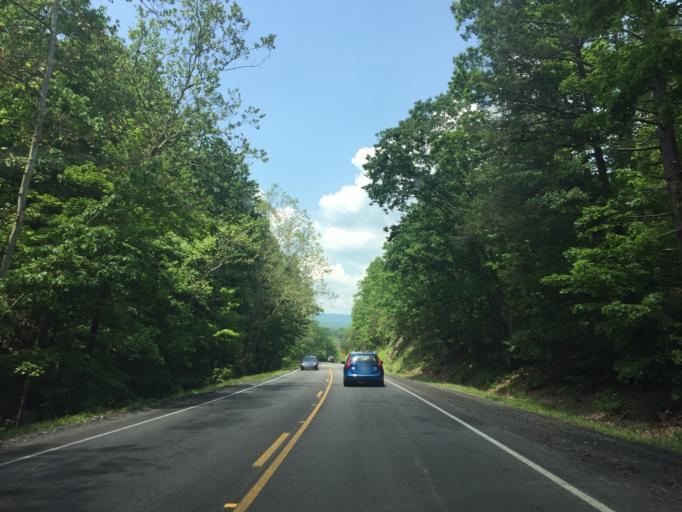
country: US
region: Virginia
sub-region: Shenandoah County
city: Woodstock
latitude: 39.0905
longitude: -78.5569
